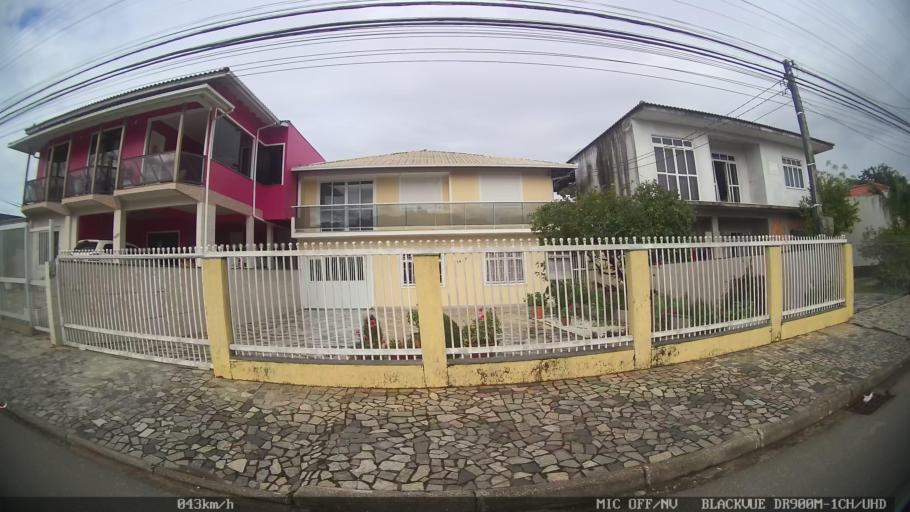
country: BR
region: Santa Catarina
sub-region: Sao Jose
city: Campinas
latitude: -27.5491
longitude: -48.6312
